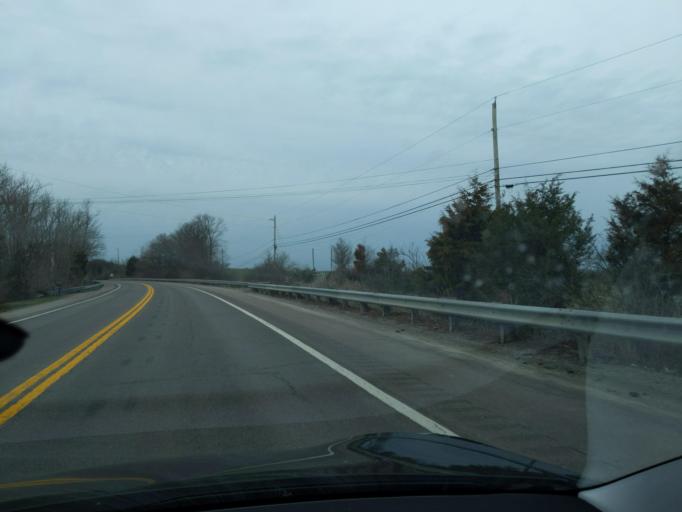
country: US
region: Kentucky
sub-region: Madison County
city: Richmond
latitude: 37.8819
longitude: -84.2941
